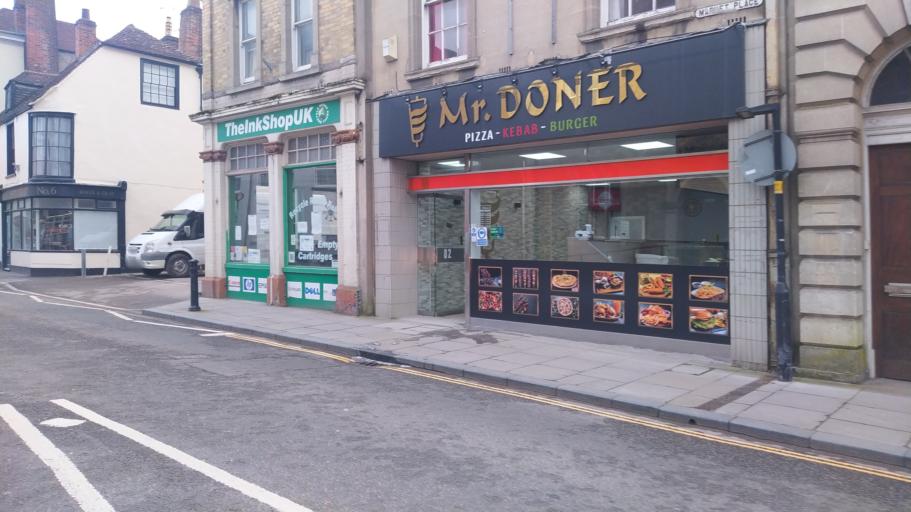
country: GB
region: England
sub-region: Wiltshire
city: Warminster
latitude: 51.2043
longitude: -2.1786
